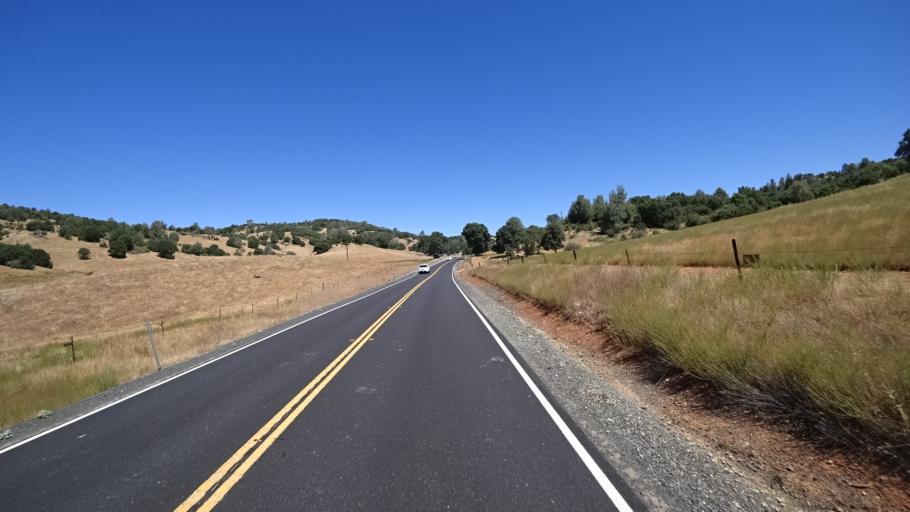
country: US
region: California
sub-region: Calaveras County
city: Copperopolis
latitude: 38.0299
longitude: -120.6474
